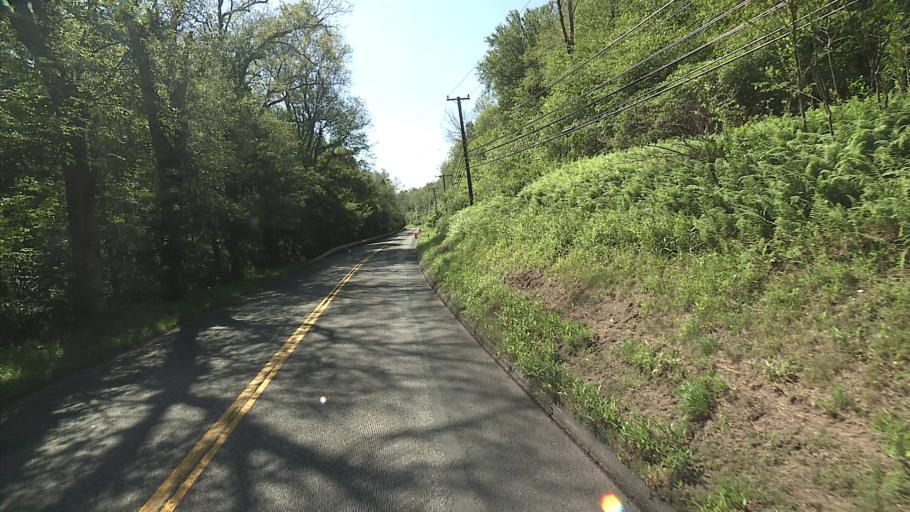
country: US
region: Connecticut
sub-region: Middlesex County
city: East Hampton
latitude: 41.5637
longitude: -72.4635
